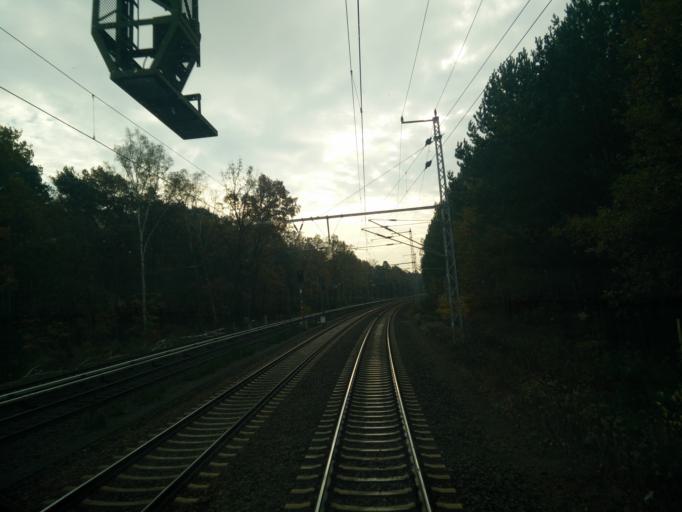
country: DE
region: Berlin
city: Bohnsdorf
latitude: 52.3960
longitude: 13.5984
